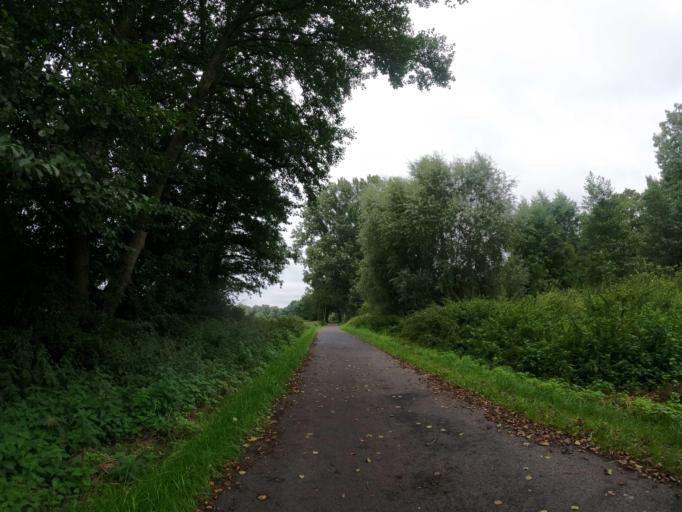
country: DE
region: Mecklenburg-Vorpommern
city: Poseritz
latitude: 54.2838
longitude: 13.2330
